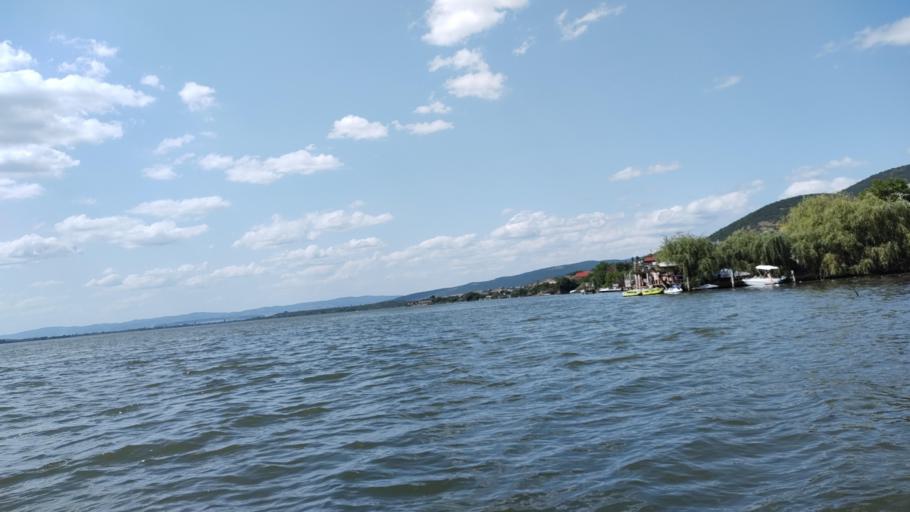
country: RO
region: Caras-Severin
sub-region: Comuna Pescari
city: Coronini
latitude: 44.6761
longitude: 21.6792
